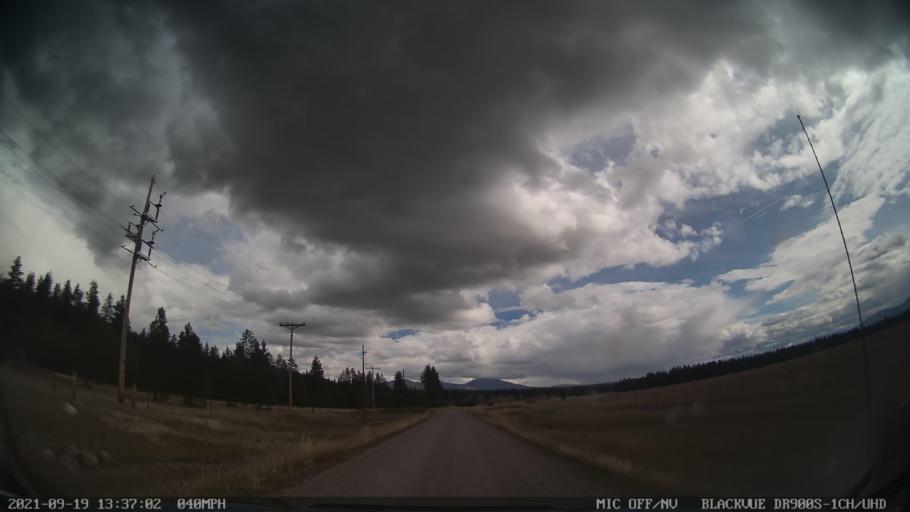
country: US
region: Montana
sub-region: Missoula County
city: Seeley Lake
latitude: 47.1066
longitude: -113.2895
